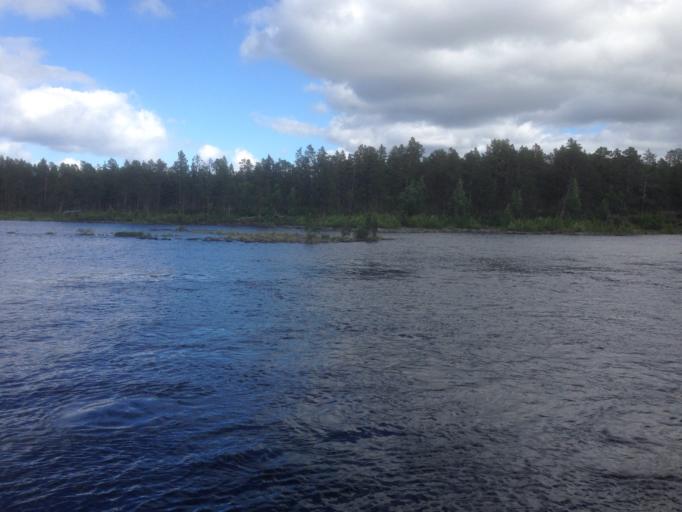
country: SE
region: Norrbotten
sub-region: Arjeplogs Kommun
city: Arjeplog
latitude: 66.4268
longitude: 16.9409
